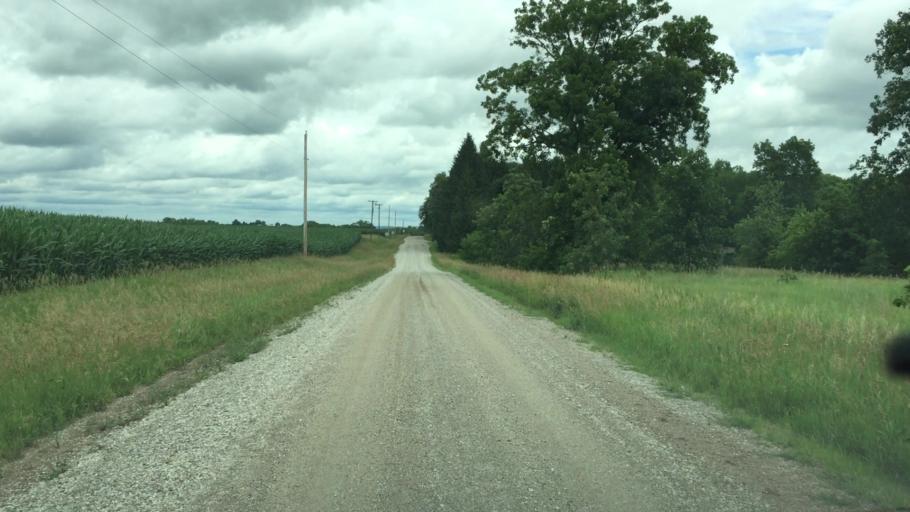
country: US
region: Iowa
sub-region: Jasper County
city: Monroe
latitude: 41.5932
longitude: -93.1161
